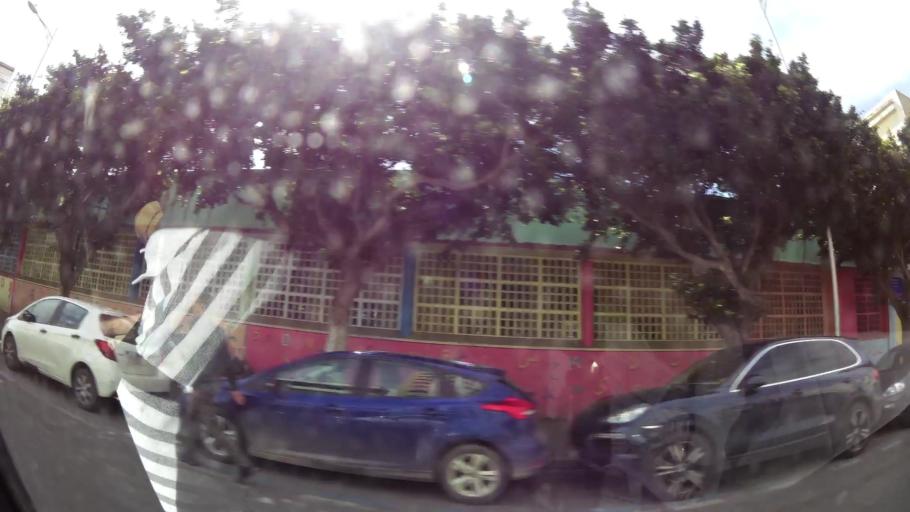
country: MA
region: Grand Casablanca
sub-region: Casablanca
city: Casablanca
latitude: 33.5923
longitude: -7.5993
